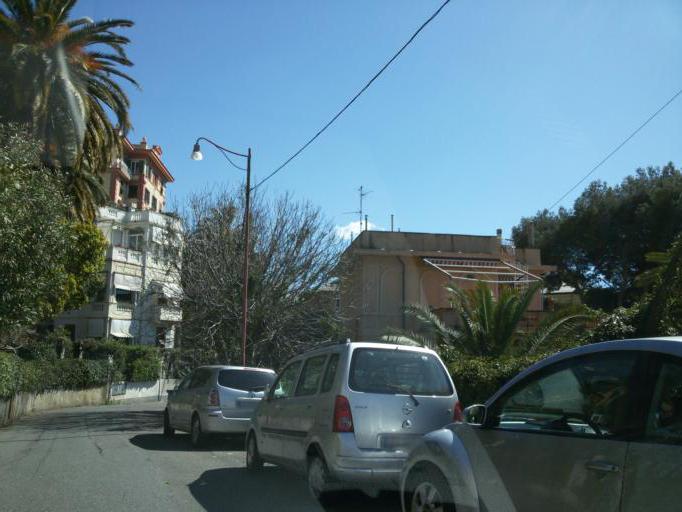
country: IT
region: Liguria
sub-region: Provincia di Genova
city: Bogliasco
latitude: 44.3865
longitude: 9.0222
